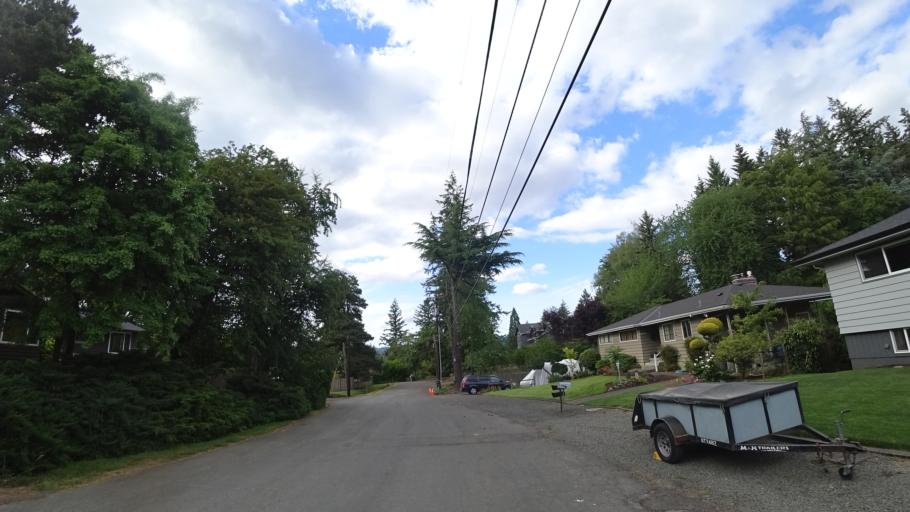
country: US
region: Oregon
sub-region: Washington County
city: Garden Home-Whitford
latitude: 45.4687
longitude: -122.7267
